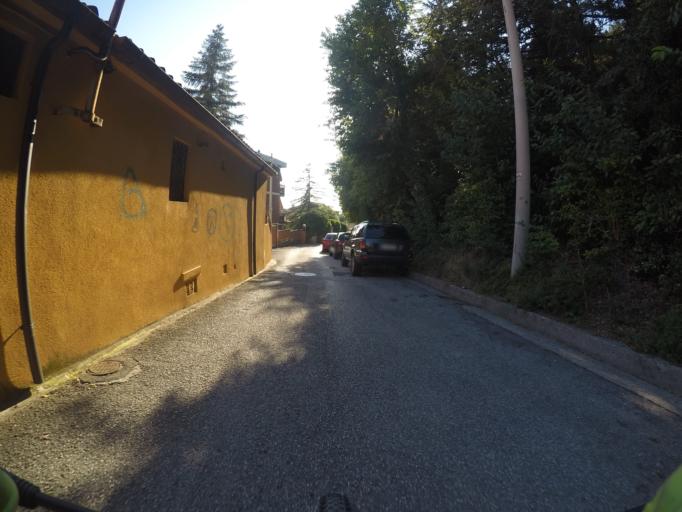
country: IT
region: Friuli Venezia Giulia
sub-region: Provincia di Trieste
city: Trieste
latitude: 45.6443
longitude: 13.8099
